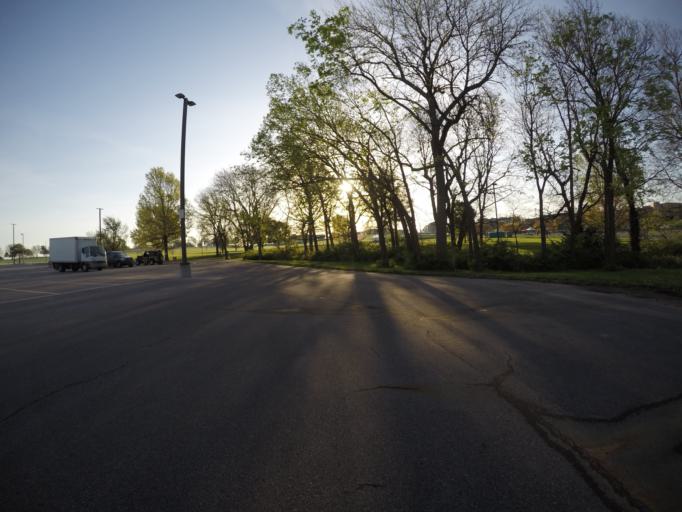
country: US
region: Missouri
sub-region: Jackson County
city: Lees Summit
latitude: 38.9113
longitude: -94.4555
